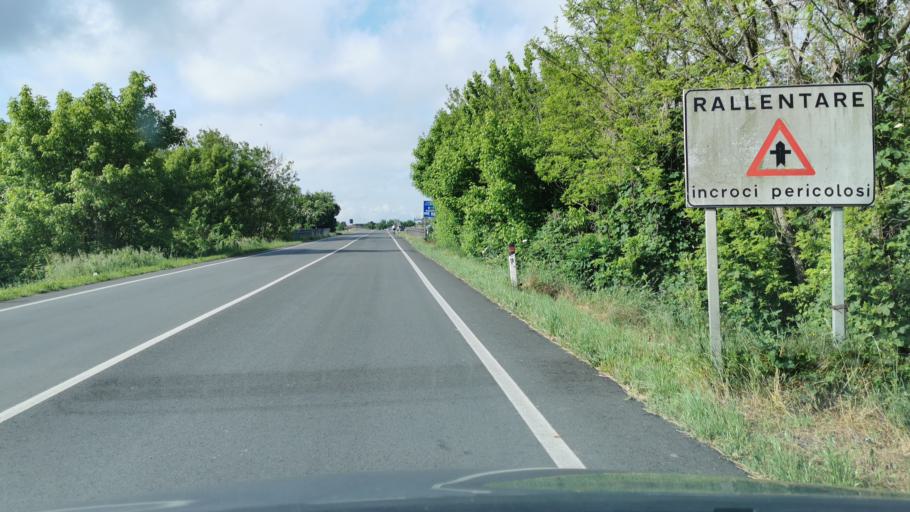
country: IT
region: Piedmont
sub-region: Provincia di Torino
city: Santena
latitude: 44.9454
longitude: 7.7825
